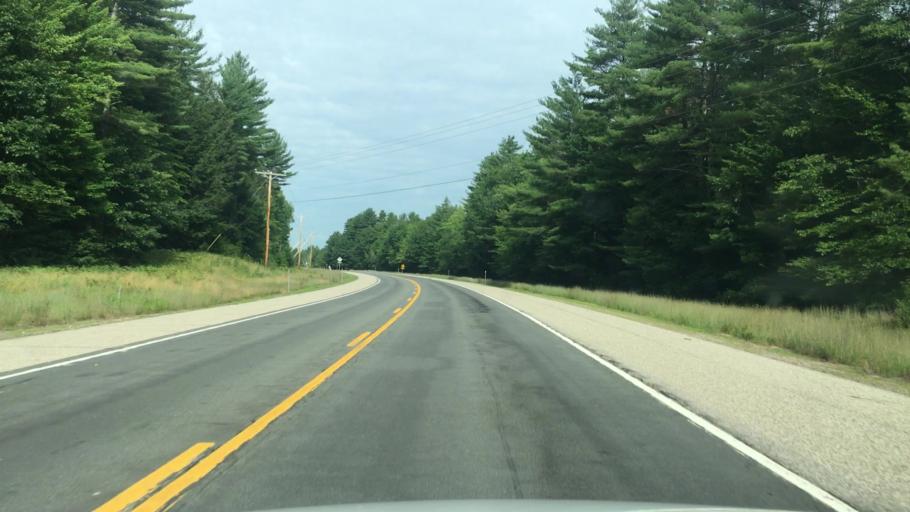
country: US
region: New Hampshire
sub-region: Carroll County
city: Tamworth
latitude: 43.8238
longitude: -71.2255
